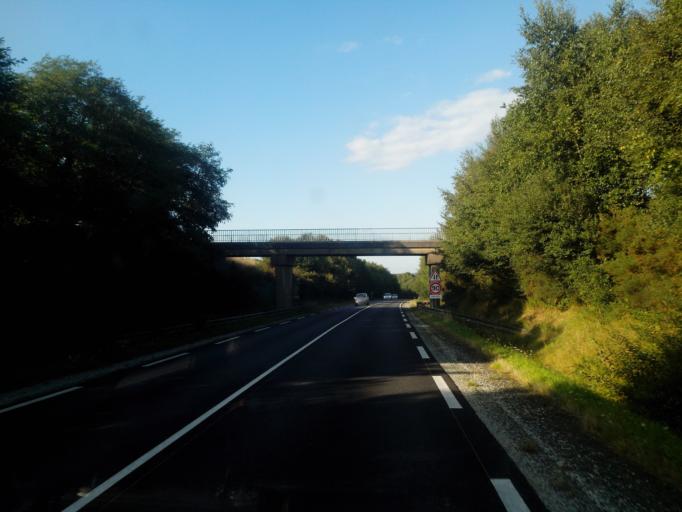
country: FR
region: Brittany
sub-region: Departement du Morbihan
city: Saint-Thuriau
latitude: 48.0158
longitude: -2.9716
